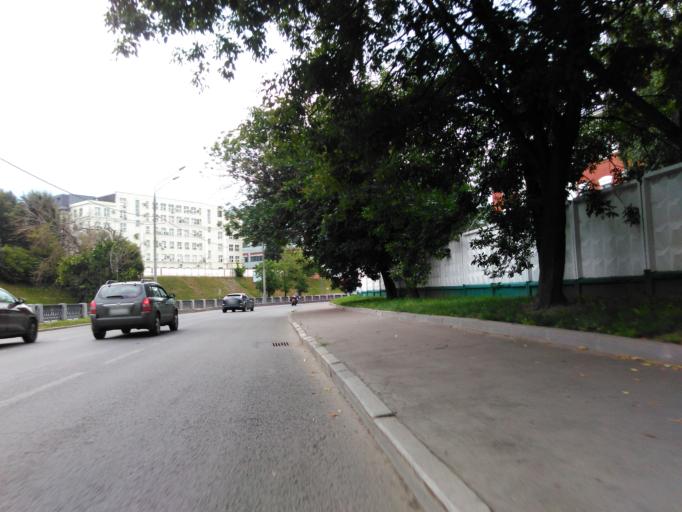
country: RU
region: Moskovskaya
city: Bogorodskoye
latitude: 55.7938
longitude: 37.7046
